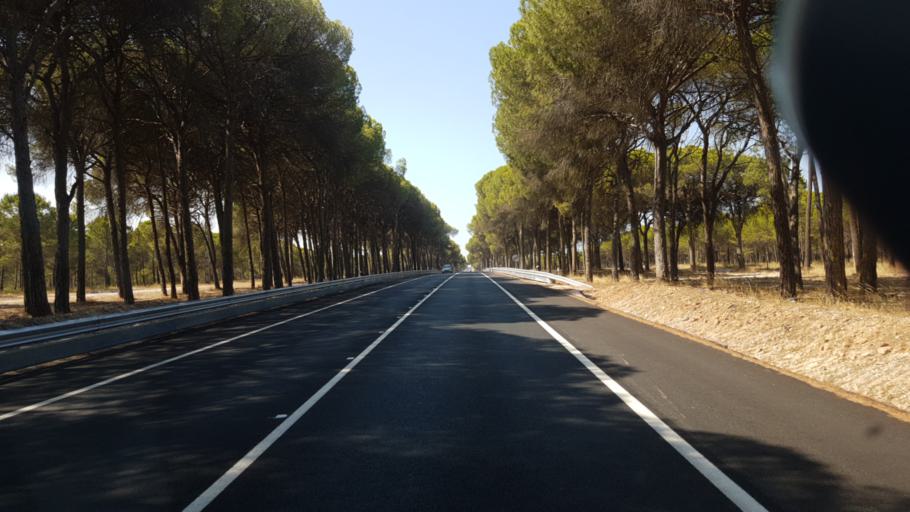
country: PT
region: Setubal
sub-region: Alcacer do Sal
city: Alcacer do Sal
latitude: 38.3355
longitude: -8.5215
